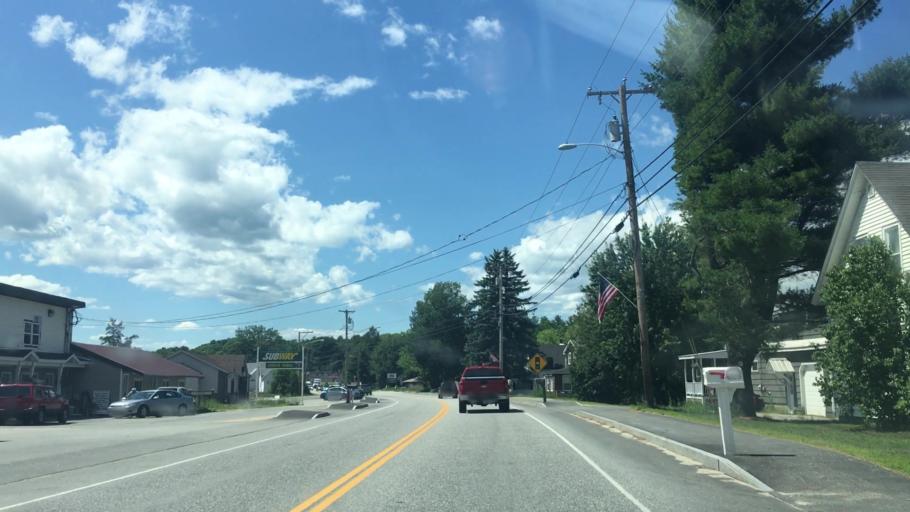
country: US
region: Maine
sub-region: Franklin County
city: Jay
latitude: 44.5016
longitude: -70.2108
